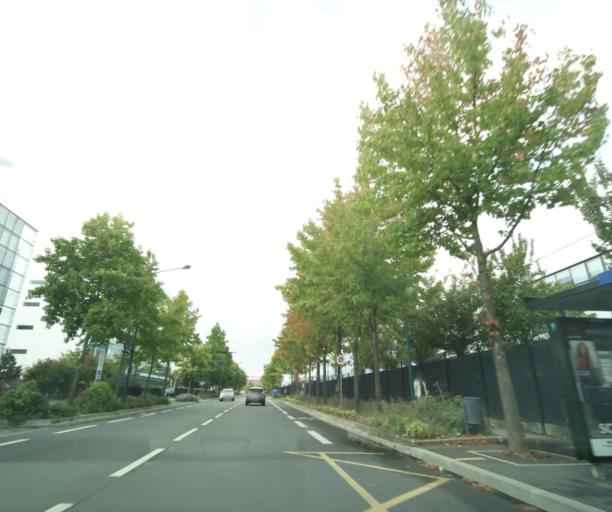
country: FR
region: Ile-de-France
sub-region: Departement de l'Essonne
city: Bievres
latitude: 48.7779
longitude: 2.2397
